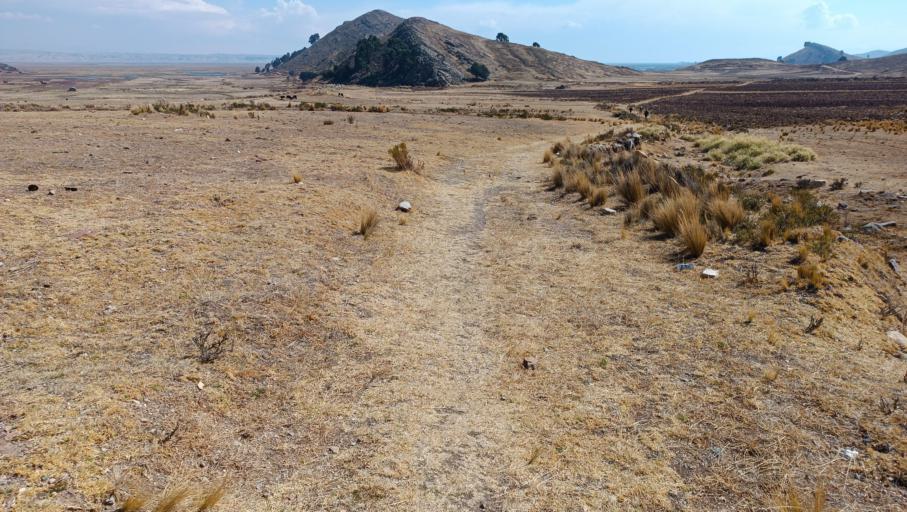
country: BO
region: La Paz
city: Batallas
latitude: -16.3477
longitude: -68.6616
